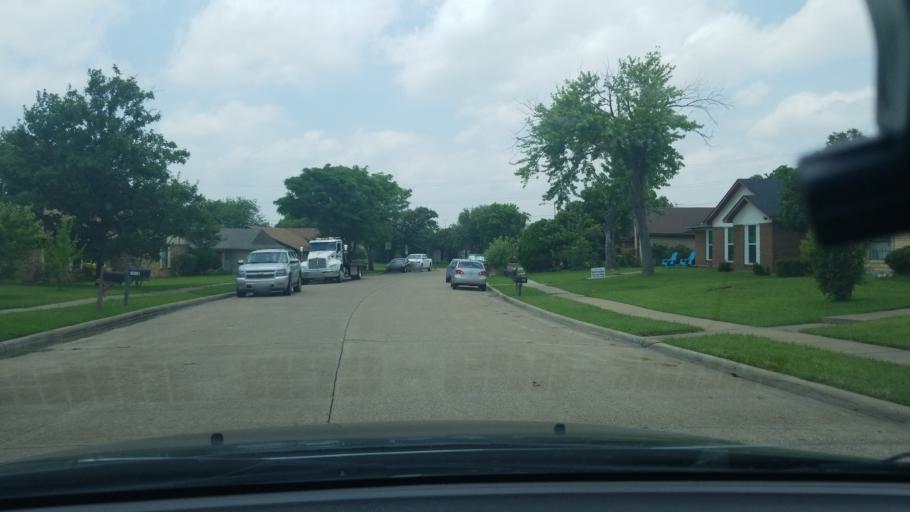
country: US
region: Texas
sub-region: Dallas County
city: Mesquite
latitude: 32.8038
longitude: -96.6192
